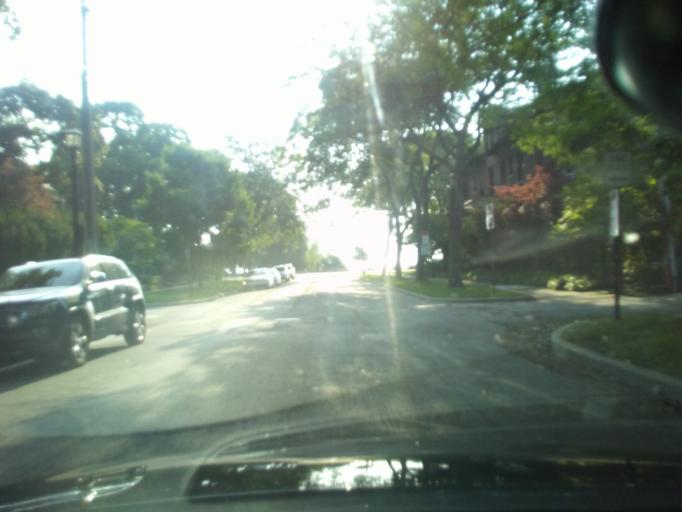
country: US
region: Illinois
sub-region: Cook County
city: Evanston
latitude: 42.0375
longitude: -87.6716
